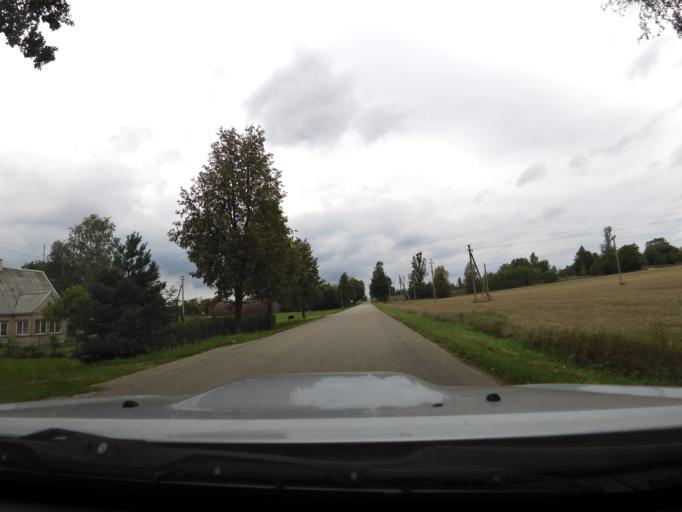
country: LT
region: Panevezys
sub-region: Birzai
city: Birzai
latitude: 56.3739
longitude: 24.7789
